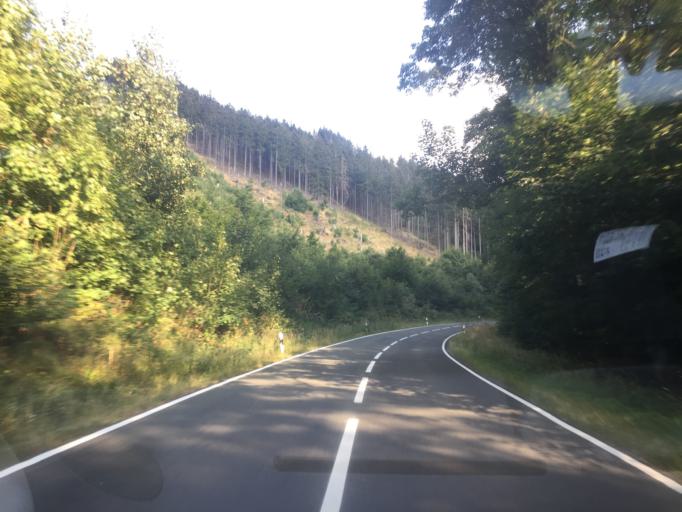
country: DE
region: Saxony-Anhalt
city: Darlingerode
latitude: 51.8012
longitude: 10.7333
